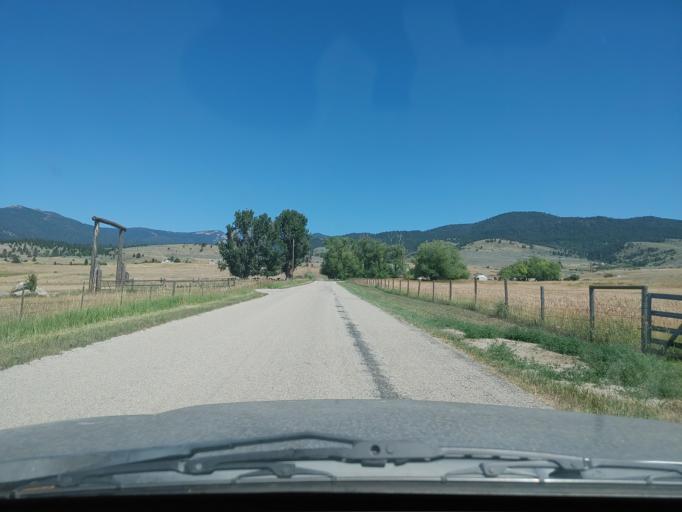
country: US
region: Montana
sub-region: Ravalli County
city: Hamilton
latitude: 46.2766
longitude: -114.0323
